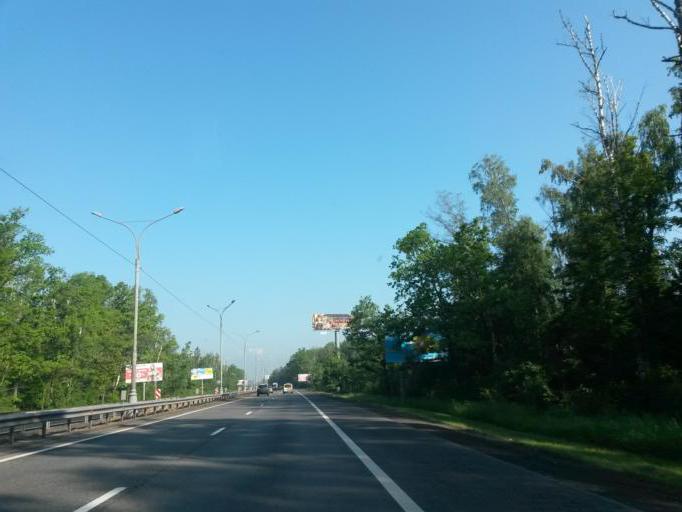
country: RU
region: Moskovskaya
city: Petrovskaya
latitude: 55.5476
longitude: 37.7943
